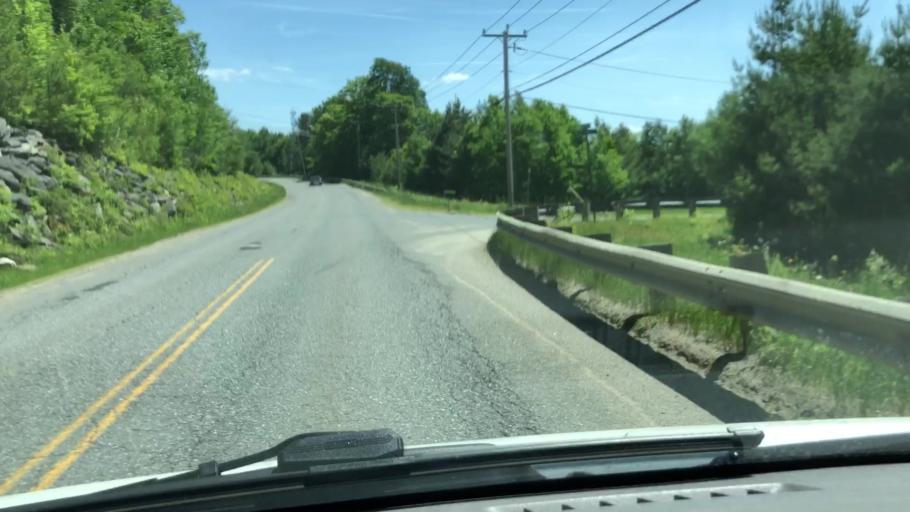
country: US
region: Massachusetts
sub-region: Franklin County
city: Charlemont
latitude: 42.5211
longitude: -72.9259
